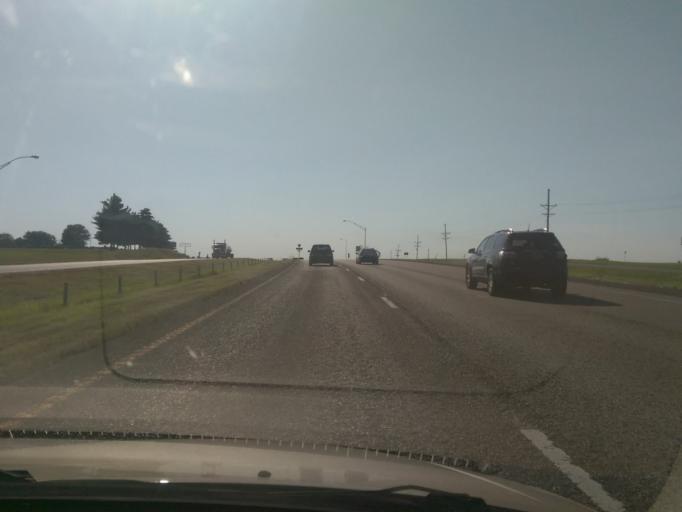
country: US
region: Missouri
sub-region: Lafayette County
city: Concordia
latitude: 38.9913
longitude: -93.5616
